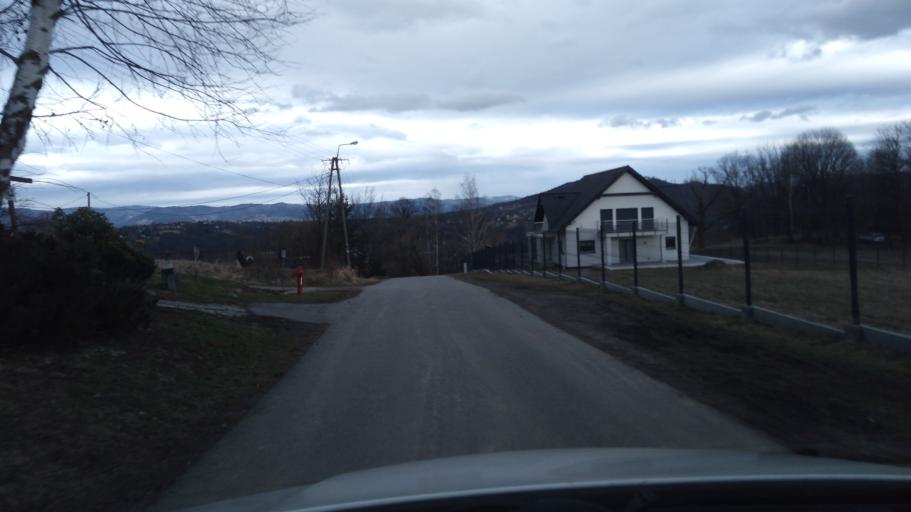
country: PL
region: Silesian Voivodeship
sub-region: Powiat zywiecki
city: Trzebinia
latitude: 49.6628
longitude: 19.2150
